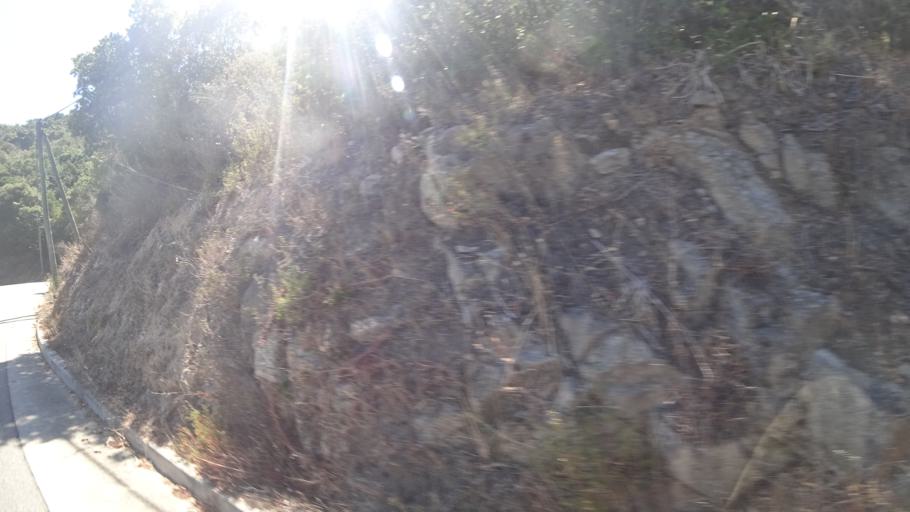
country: FR
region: Corsica
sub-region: Departement de la Corse-du-Sud
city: Alata
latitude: 41.9779
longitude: 8.6822
